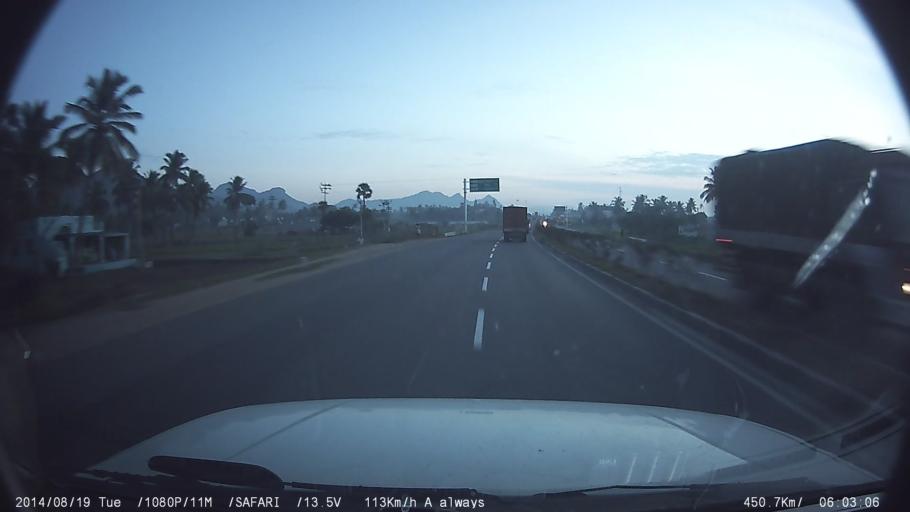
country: IN
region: Tamil Nadu
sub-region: Salem
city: Omalur
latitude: 11.8494
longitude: 78.0689
